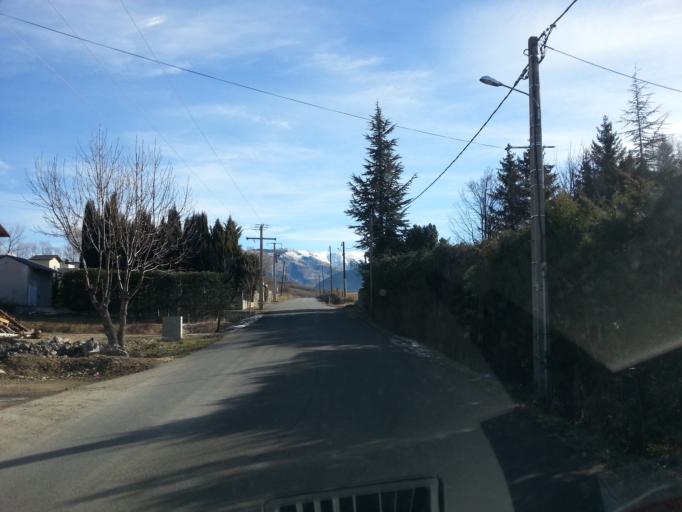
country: ES
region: Catalonia
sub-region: Provincia de Girona
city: Llivia
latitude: 42.4668
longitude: 1.9999
